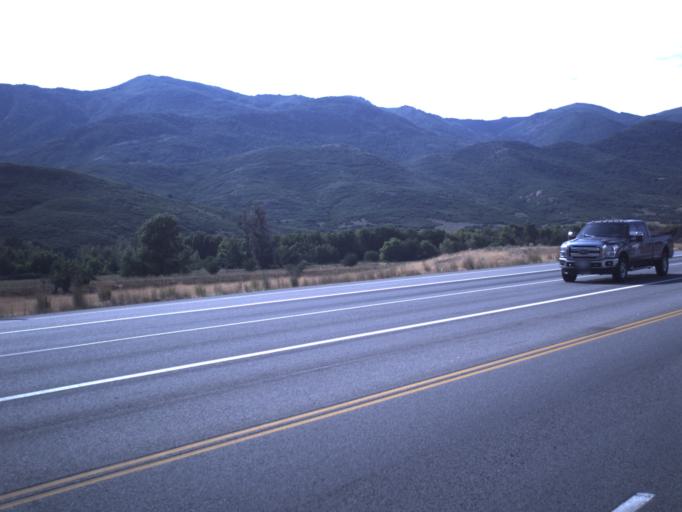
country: US
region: Utah
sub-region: Wasatch County
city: Heber
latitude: 40.5580
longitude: -111.4258
